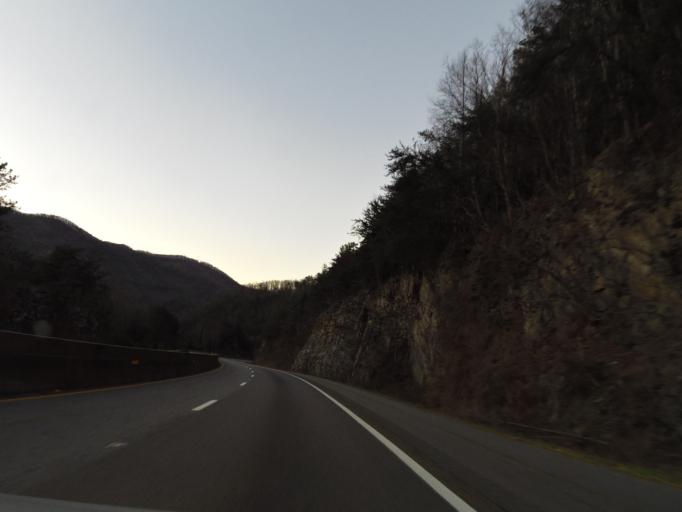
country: US
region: North Carolina
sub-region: Haywood County
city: Cove Creek
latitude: 35.7125
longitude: -83.0311
